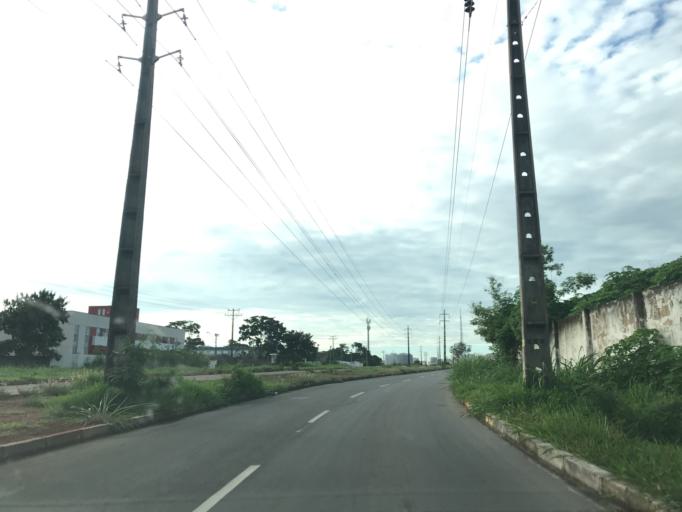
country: BR
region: Federal District
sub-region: Brasilia
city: Brasilia
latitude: -15.7718
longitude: -47.8958
